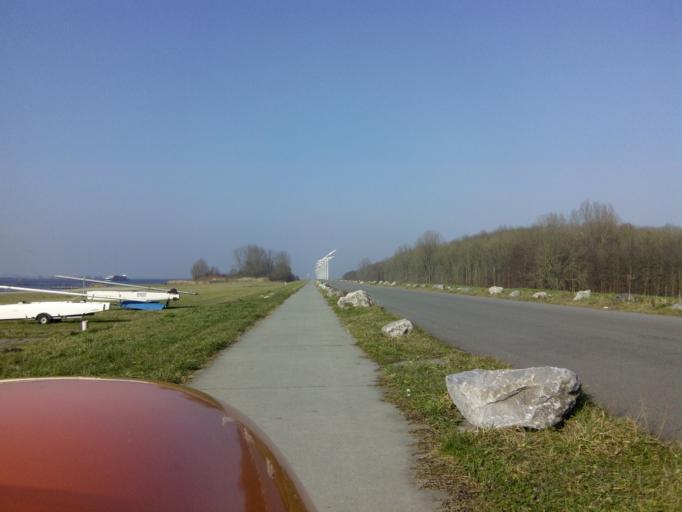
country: NL
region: Utrecht
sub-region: Gemeente Bunschoten
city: Bunschoten
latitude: 52.2596
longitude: 5.3933
